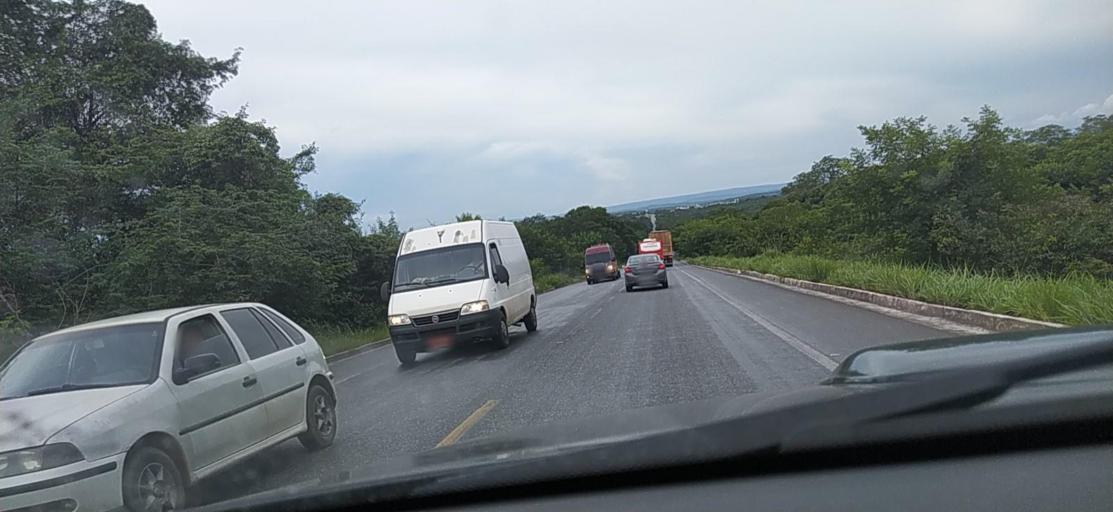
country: BR
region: Minas Gerais
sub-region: Montes Claros
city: Montes Claros
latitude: -16.6618
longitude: -43.7619
